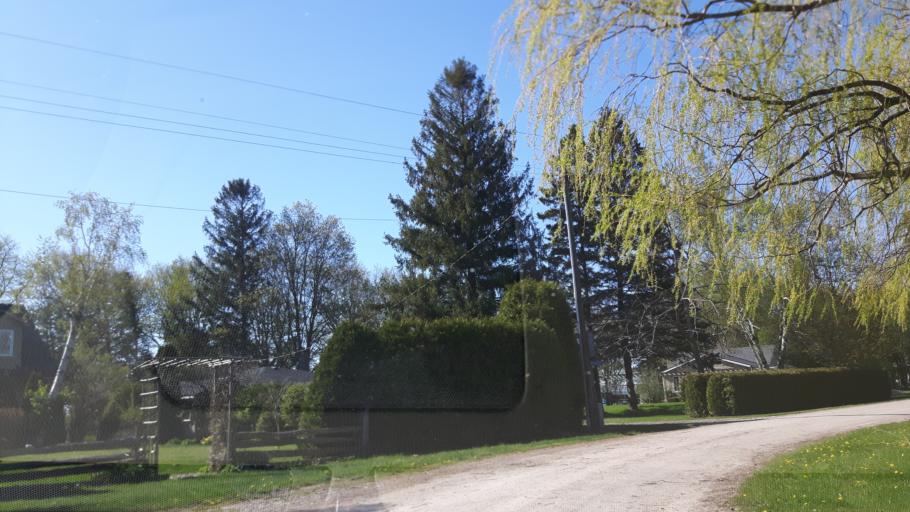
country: CA
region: Ontario
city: Bluewater
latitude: 43.5120
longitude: -81.7102
